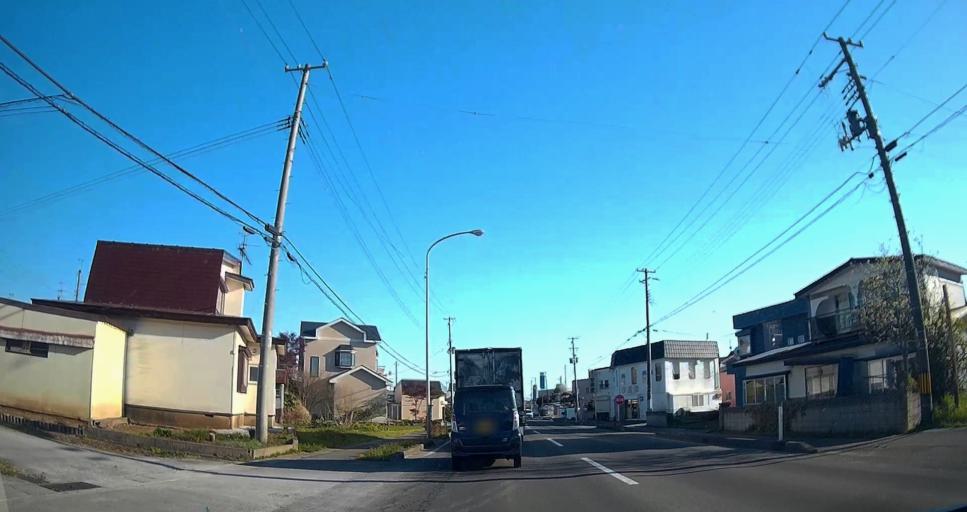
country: JP
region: Aomori
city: Mutsu
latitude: 41.2989
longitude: 141.2217
